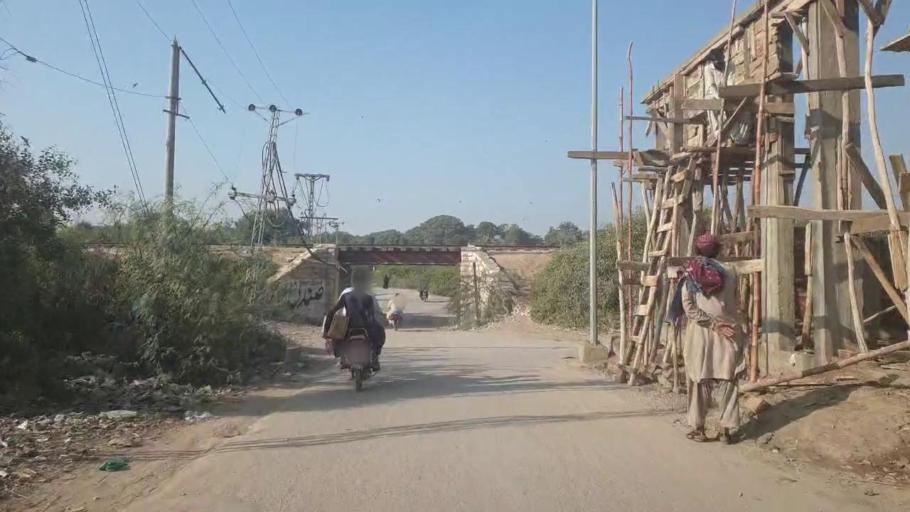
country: PK
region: Sindh
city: Kotri
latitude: 25.3682
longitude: 68.3059
